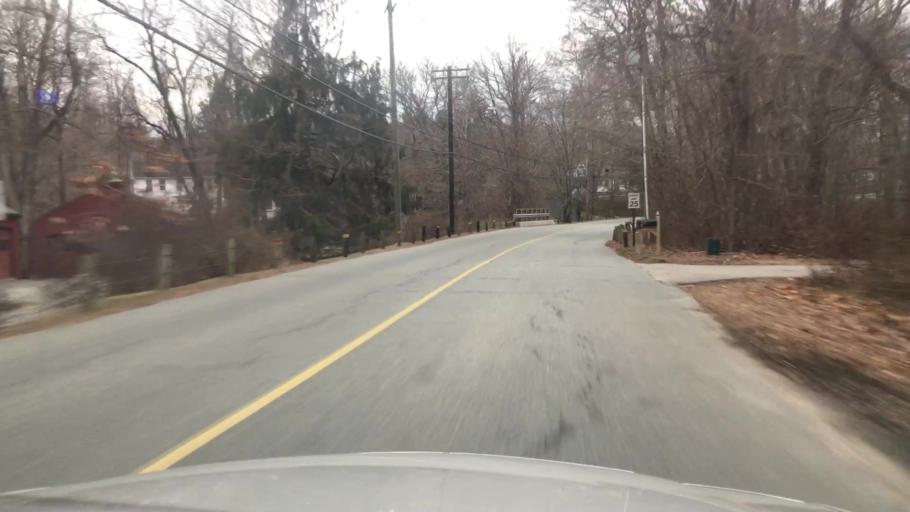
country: US
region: Connecticut
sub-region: Middlesex County
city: Essex Village
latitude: 41.3631
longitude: -72.4010
